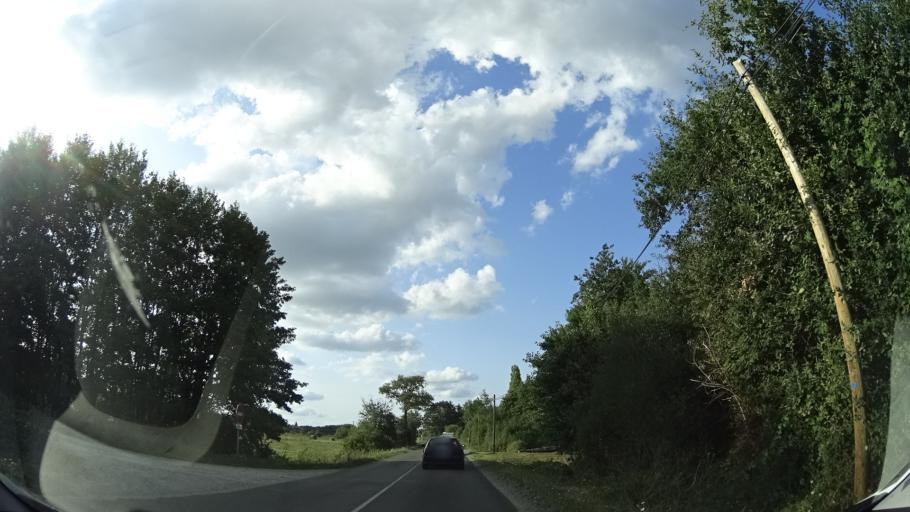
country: FR
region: Pays de la Loire
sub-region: Departement de la Loire-Atlantique
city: Casson
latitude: 47.3986
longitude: -1.5280
